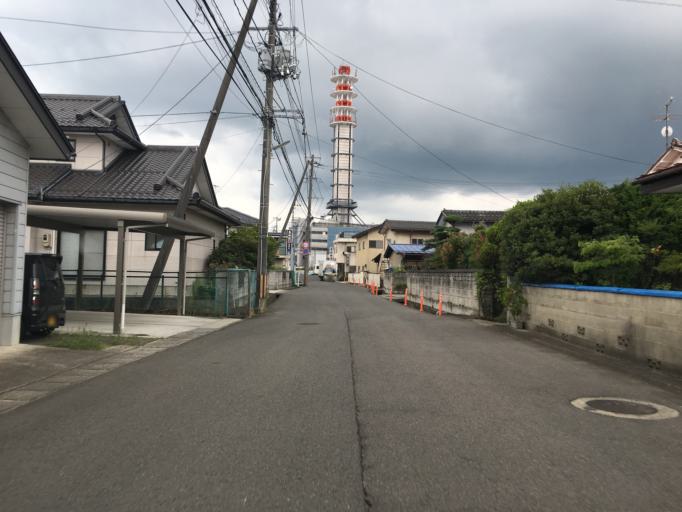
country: JP
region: Fukushima
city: Fukushima-shi
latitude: 37.7458
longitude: 140.4445
